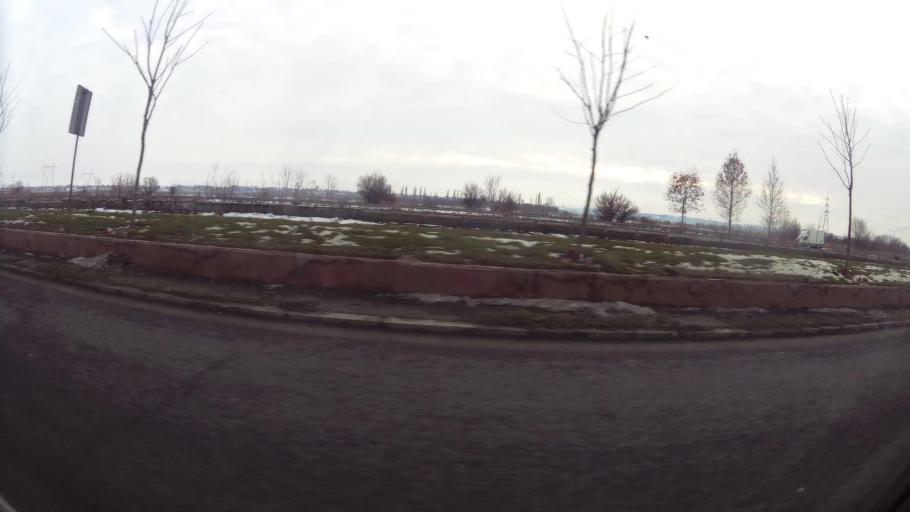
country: RO
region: Ilfov
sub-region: Comuna Popesti-Leordeni
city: Popesti-Leordeni
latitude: 44.3944
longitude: 26.1802
